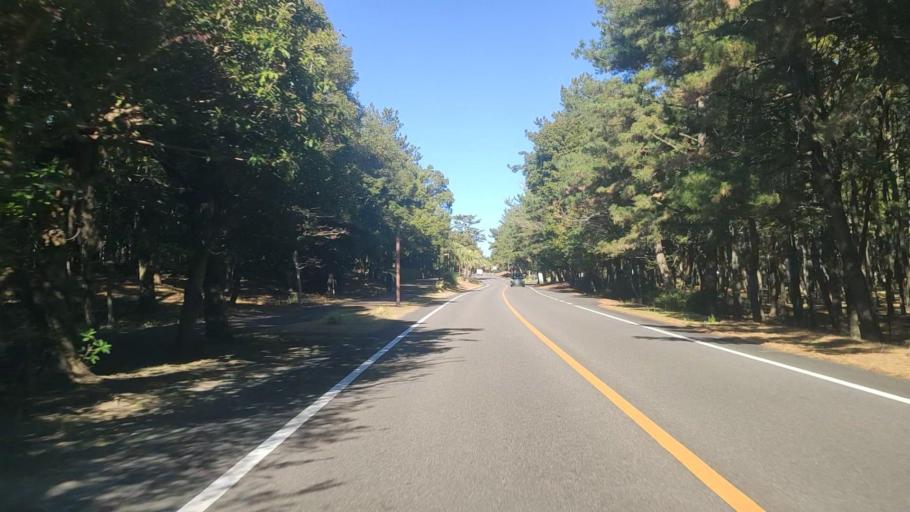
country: JP
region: Miyazaki
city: Miyazaki-shi
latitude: 31.9499
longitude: 131.4661
